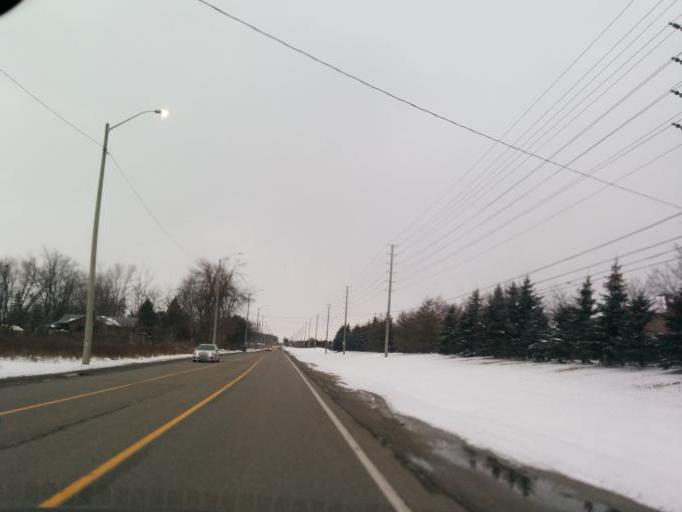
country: CA
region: Ontario
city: Mississauga
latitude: 43.5611
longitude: -79.7688
